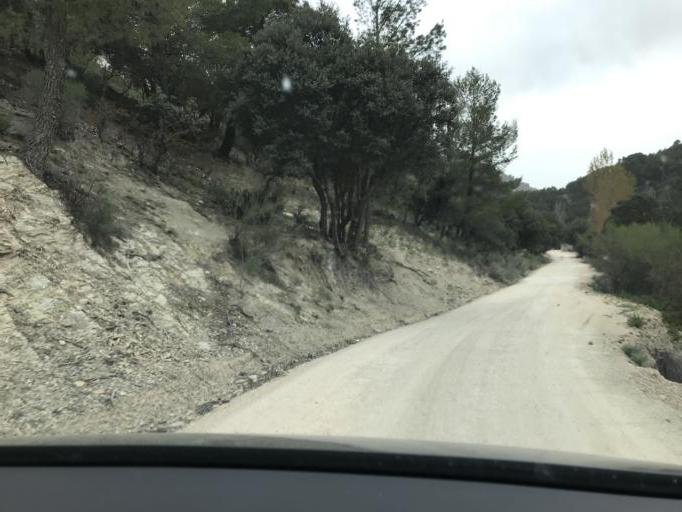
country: ES
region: Andalusia
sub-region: Provincia de Granada
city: Castril
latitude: 37.8467
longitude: -2.7748
